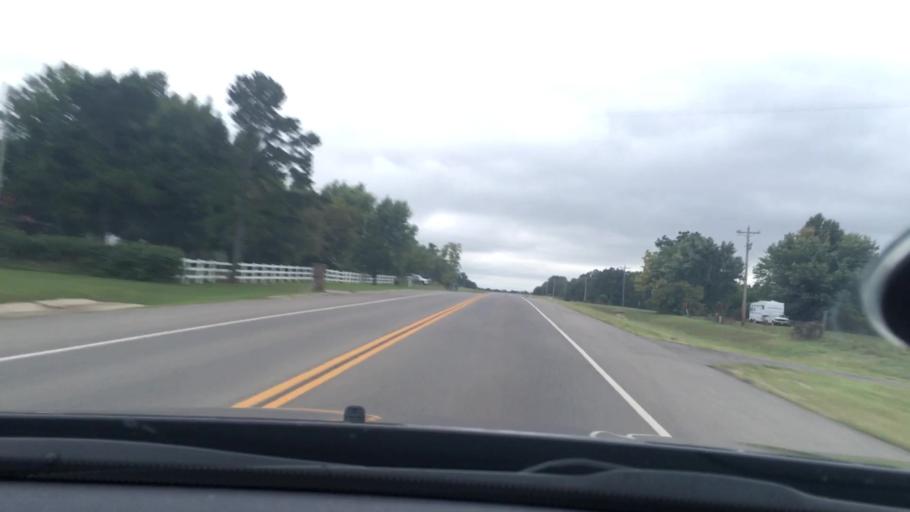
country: US
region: Oklahoma
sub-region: Sequoyah County
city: Vian
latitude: 35.6054
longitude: -94.9763
